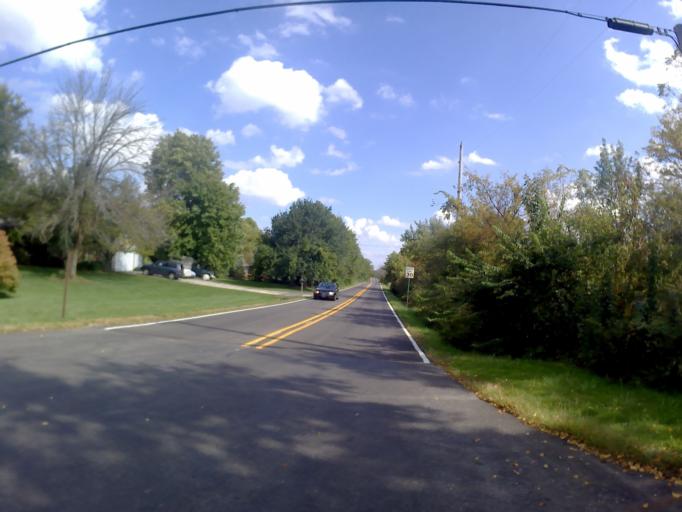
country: US
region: Illinois
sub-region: DuPage County
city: Woodridge
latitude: 41.7420
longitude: -88.0882
